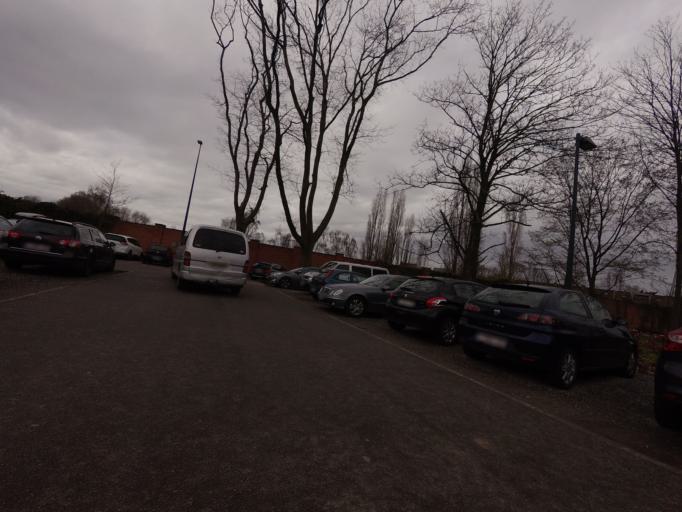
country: BE
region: Flanders
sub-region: Provincie Antwerpen
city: Lier
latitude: 51.1316
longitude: 4.5570
